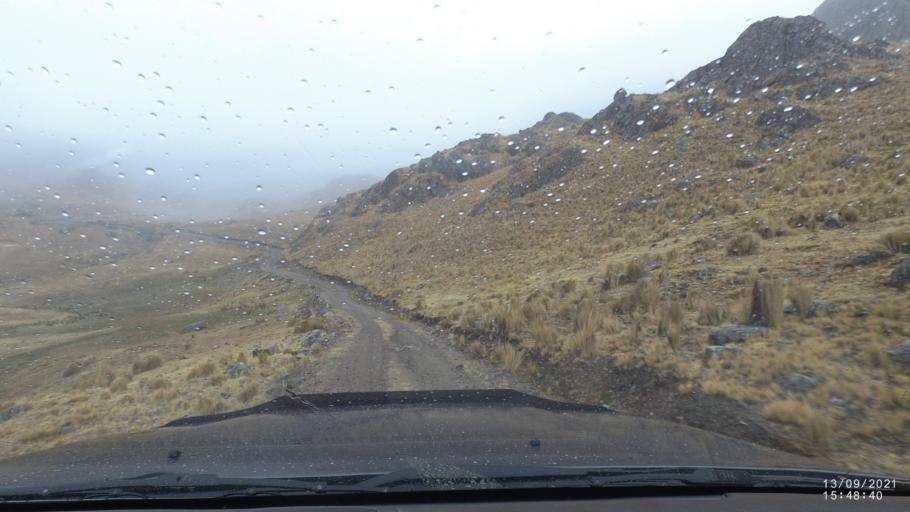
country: BO
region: Cochabamba
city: Colomi
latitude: -17.3103
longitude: -65.7154
